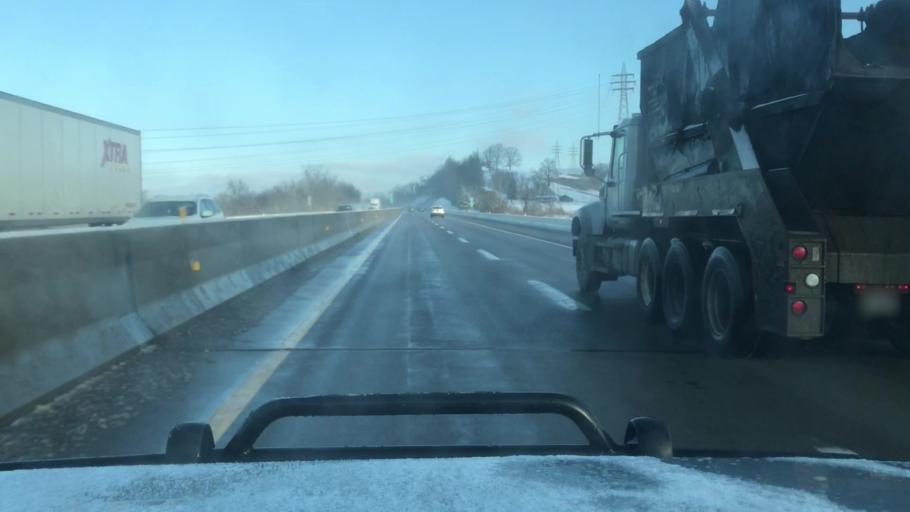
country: US
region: Pennsylvania
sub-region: Allegheny County
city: Plum
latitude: 40.4937
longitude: -79.7828
